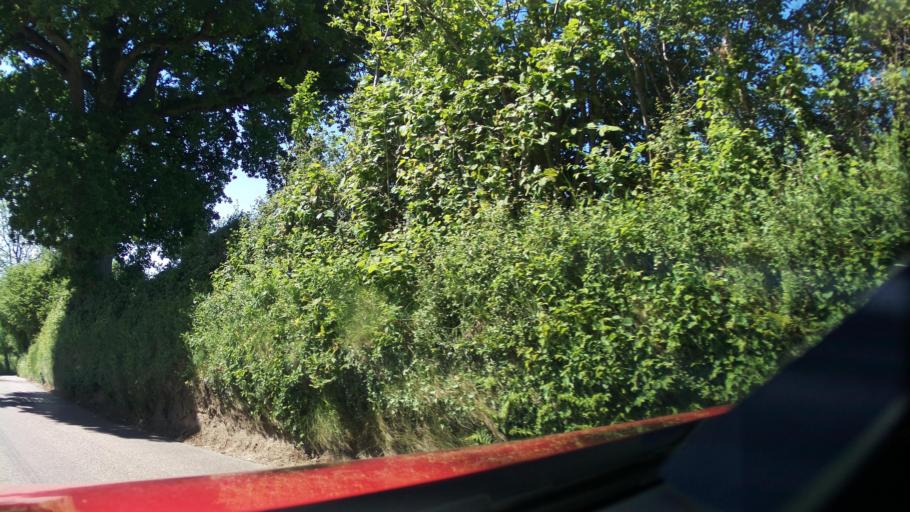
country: GB
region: England
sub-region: Devon
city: Ottery St Mary
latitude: 50.7304
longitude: -3.2774
